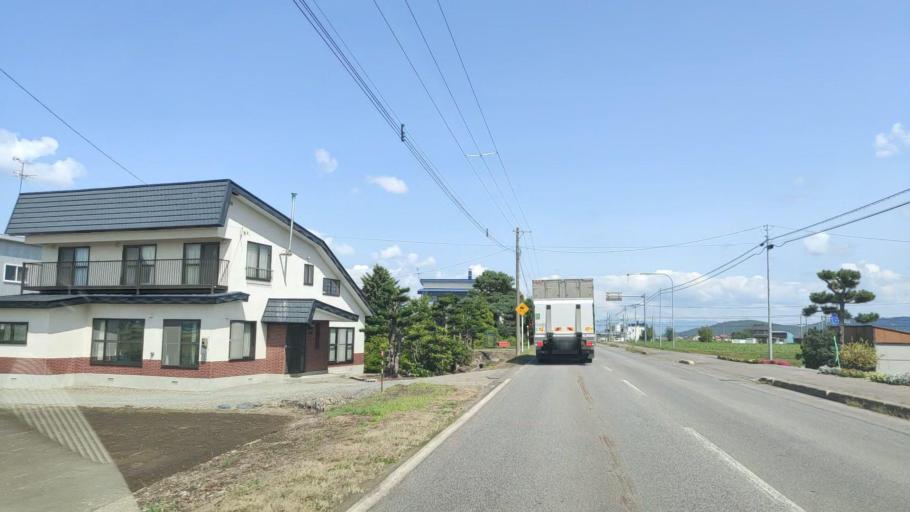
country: JP
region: Hokkaido
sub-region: Asahikawa-shi
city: Asahikawa
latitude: 43.7230
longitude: 142.4581
